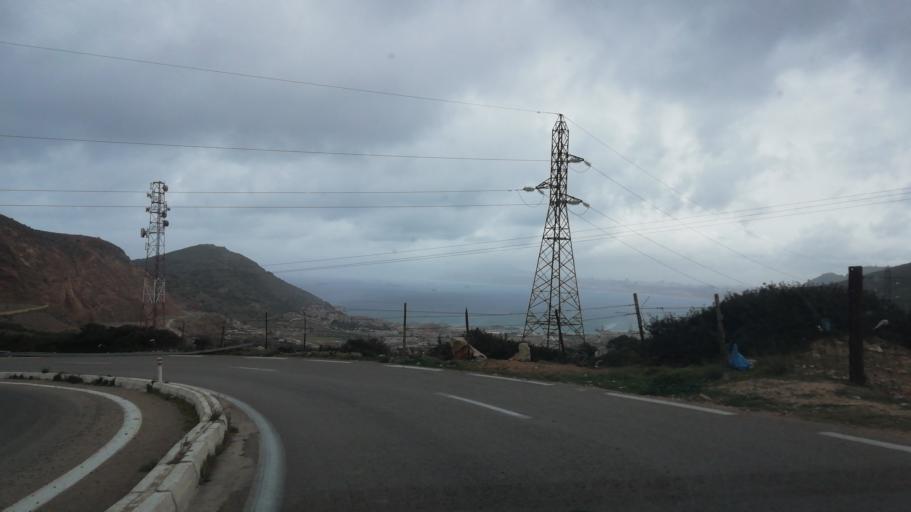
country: DZ
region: Oran
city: Mers el Kebir
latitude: 35.7195
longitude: -0.7354
